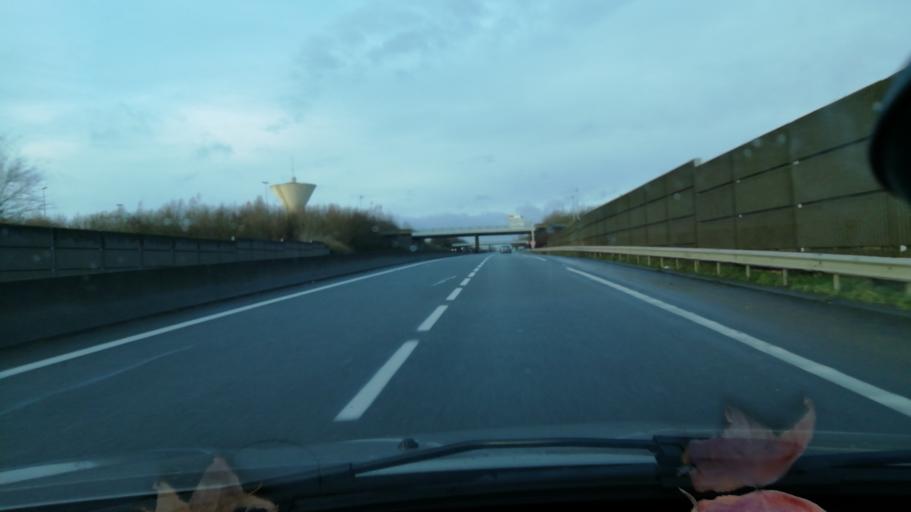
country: FR
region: Nord-Pas-de-Calais
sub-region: Departement du Nord
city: Hautmont
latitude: 50.2648
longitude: 3.9250
